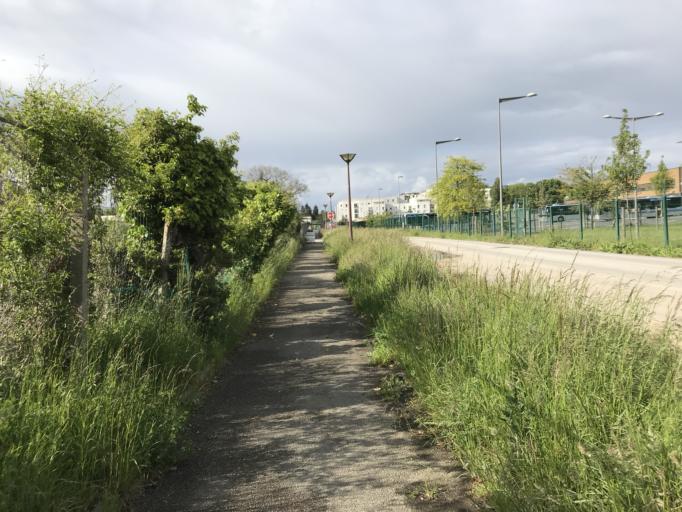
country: FR
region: Ile-de-France
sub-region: Departement des Yvelines
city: Velizy-Villacoublay
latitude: 48.7780
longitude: 2.1913
